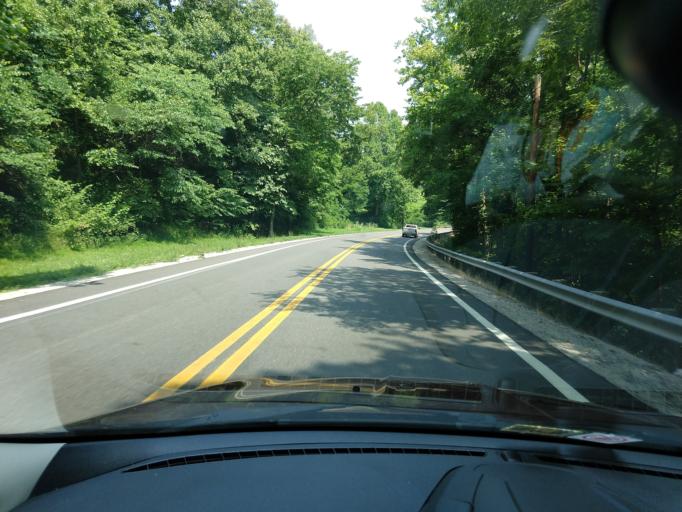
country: US
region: West Virginia
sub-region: Jackson County
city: Ravenswood
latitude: 38.8726
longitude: -81.8763
